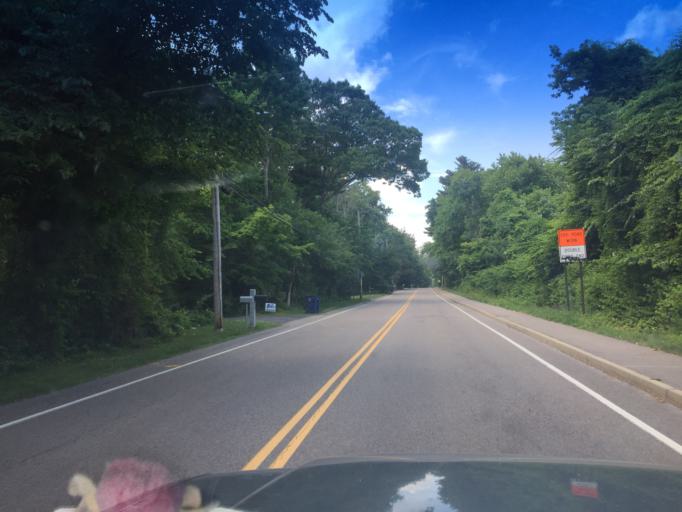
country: US
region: Massachusetts
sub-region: Norfolk County
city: Medway
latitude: 42.1504
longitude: -71.4195
